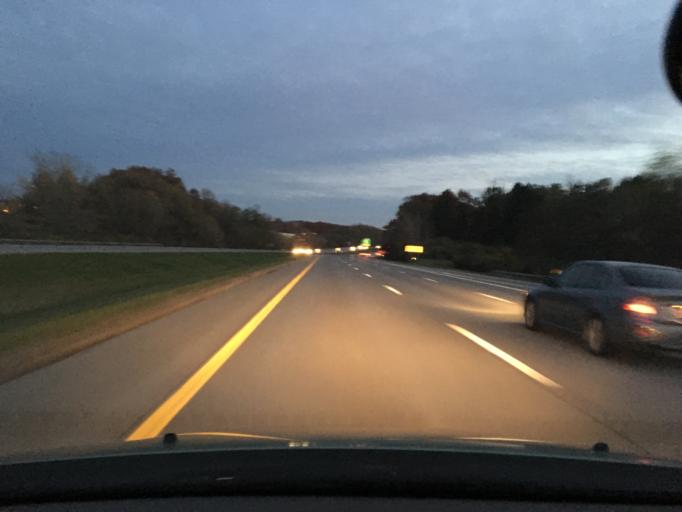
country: US
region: New York
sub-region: Ontario County
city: Victor
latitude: 43.0287
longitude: -77.4510
